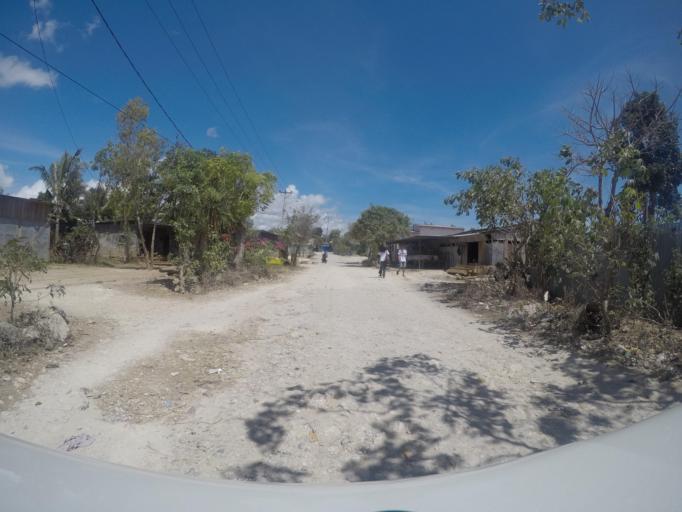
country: TL
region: Baucau
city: Baucau
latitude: -8.4839
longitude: 126.4519
